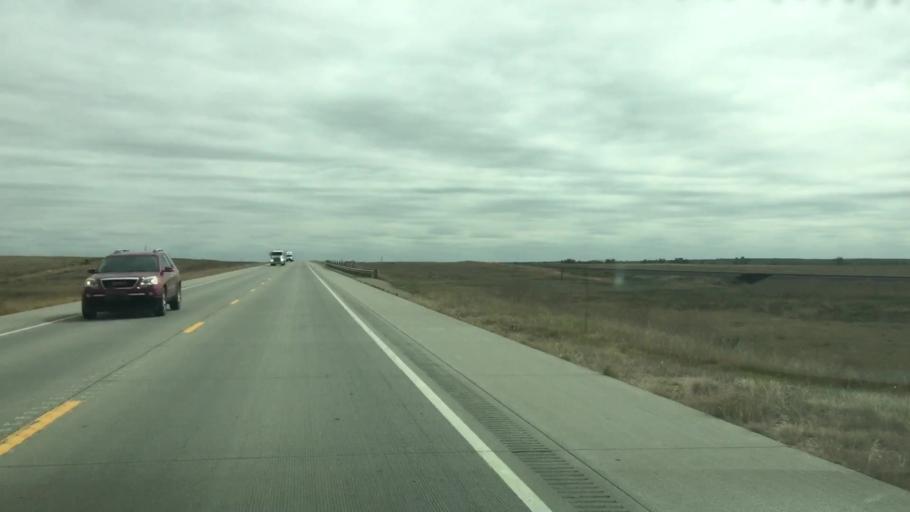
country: US
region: Colorado
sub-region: Kiowa County
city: Eads
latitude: 38.7761
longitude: -102.8848
